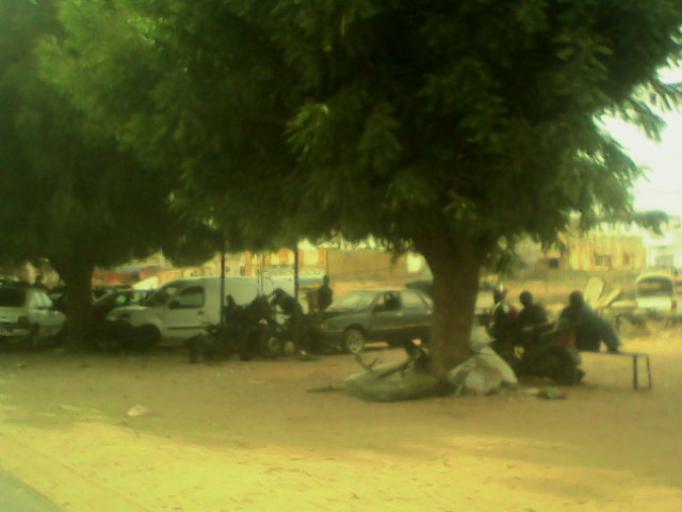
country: SN
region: Diourbel
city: Touba
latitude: 14.8818
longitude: -15.8891
